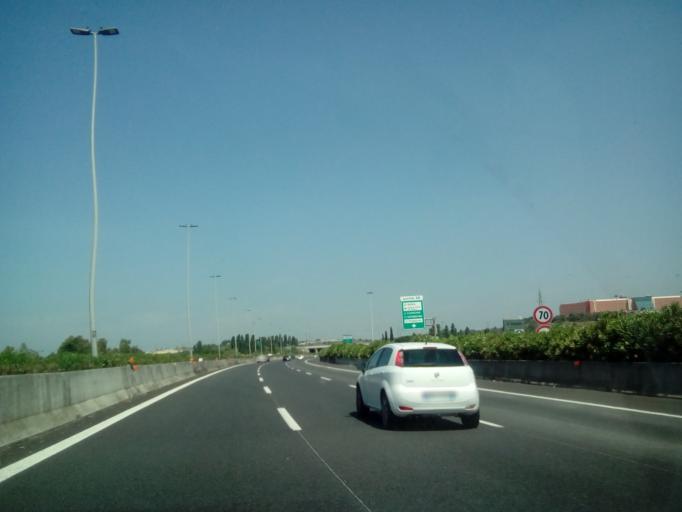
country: IT
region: Latium
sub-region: Citta metropolitana di Roma Capitale
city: Vitinia
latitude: 41.8142
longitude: 12.3945
